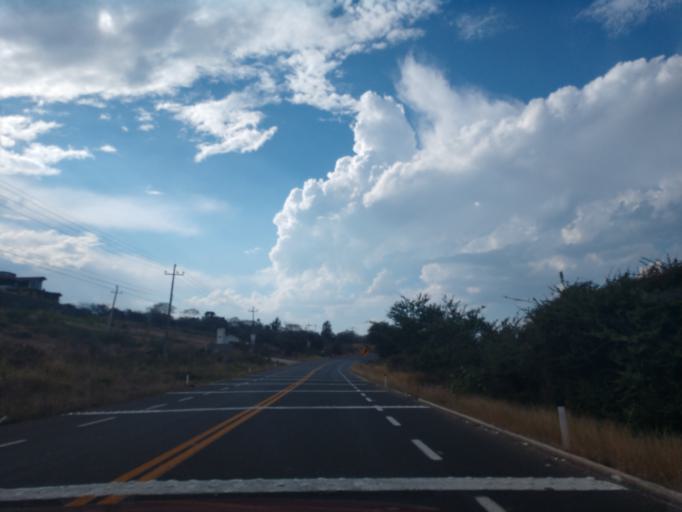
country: MX
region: Jalisco
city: Ajijic
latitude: 20.1868
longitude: -103.2526
